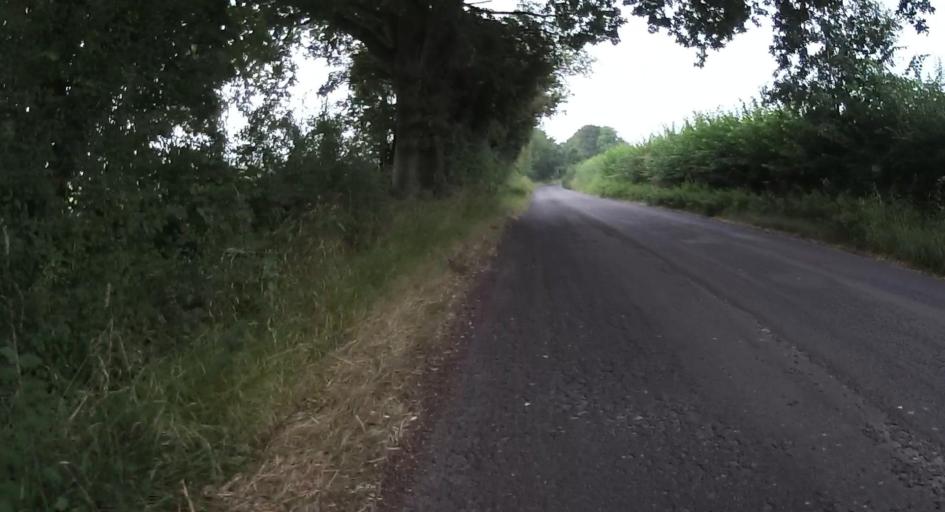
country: GB
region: England
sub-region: Hampshire
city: Old Basing
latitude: 51.2532
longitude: -1.0430
